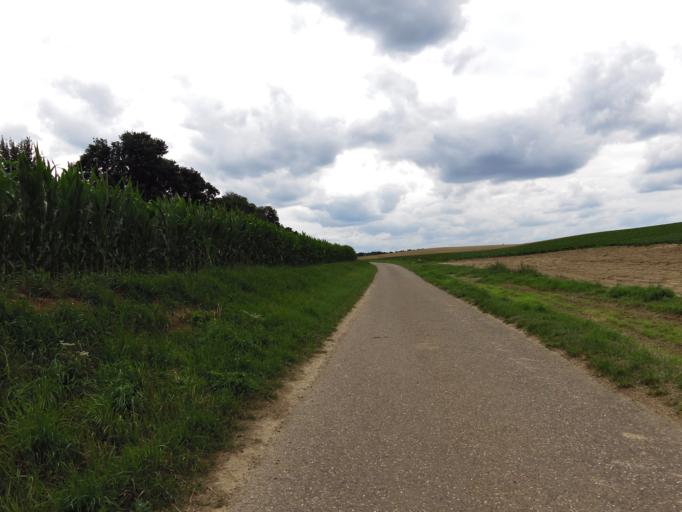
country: NL
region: Limburg
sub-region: Gemeente Schinnen
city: Doenrade
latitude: 50.9632
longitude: 5.9235
